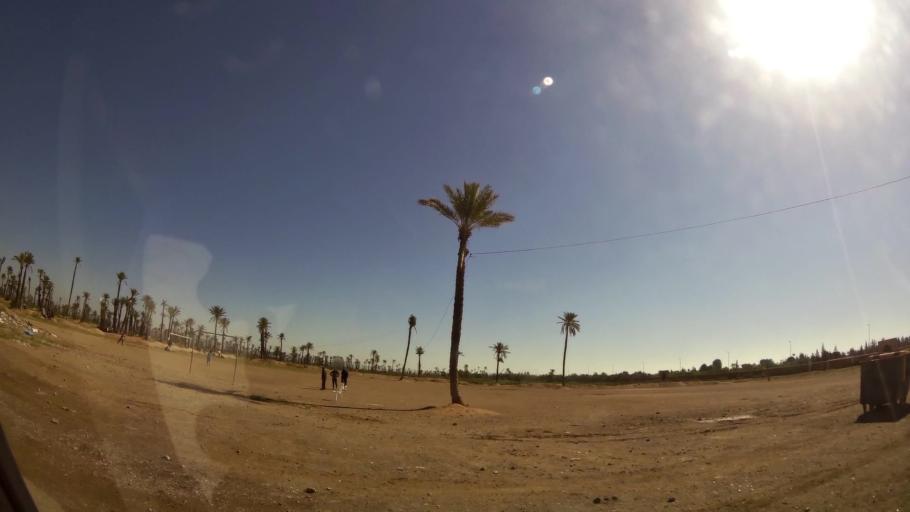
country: MA
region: Marrakech-Tensift-Al Haouz
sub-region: Marrakech
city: Marrakesh
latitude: 31.6570
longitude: -7.9529
